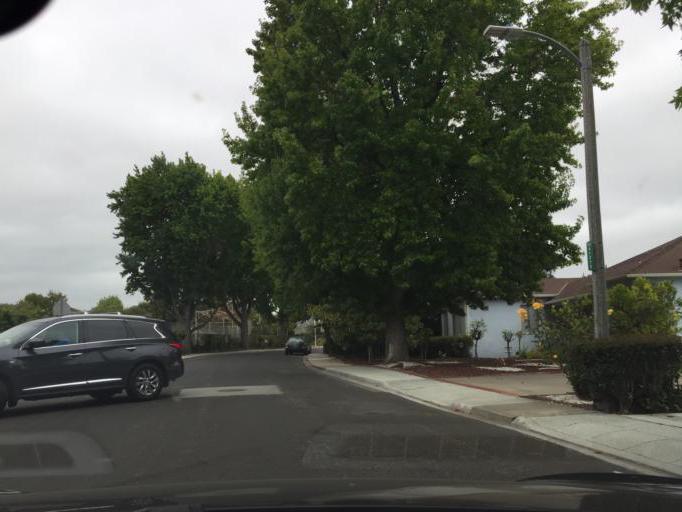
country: US
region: California
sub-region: San Mateo County
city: Burlingame
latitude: 37.5891
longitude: -122.3769
